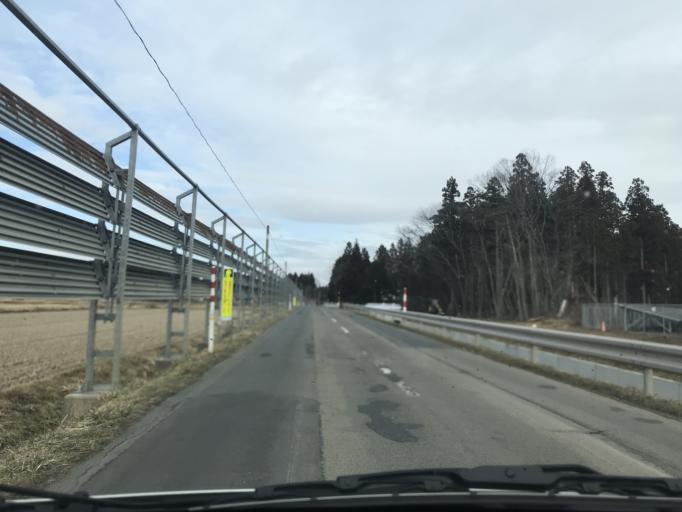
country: JP
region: Iwate
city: Kitakami
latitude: 39.3318
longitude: 141.0274
